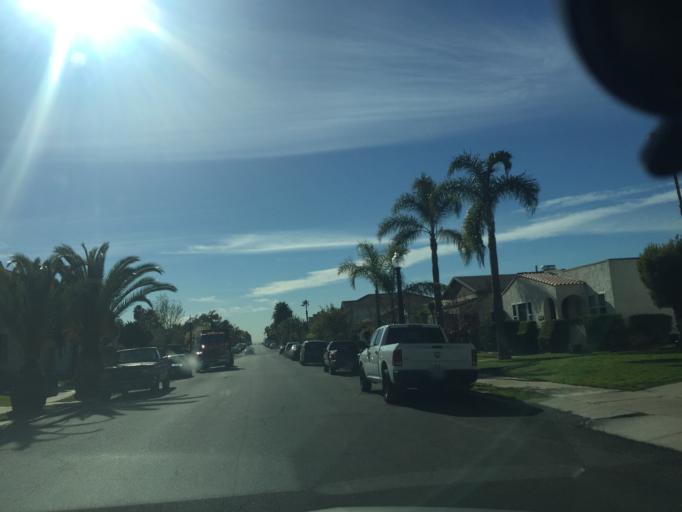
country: US
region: California
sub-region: San Diego County
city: Lemon Grove
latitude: 32.7601
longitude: -117.0868
